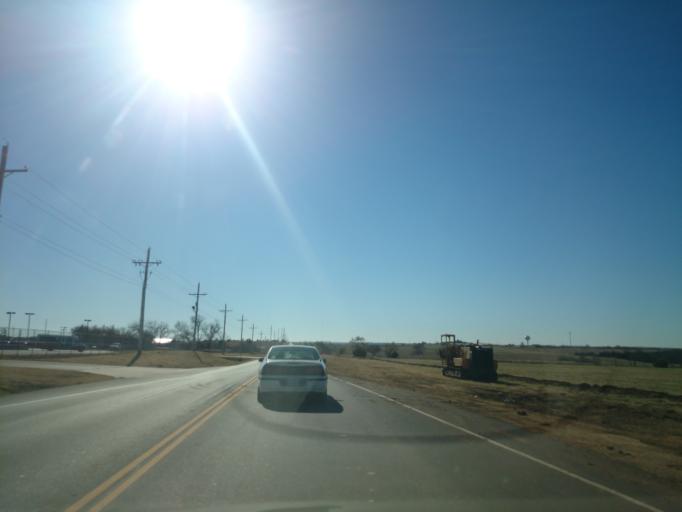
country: US
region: Oklahoma
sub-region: Payne County
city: Stillwater
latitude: 36.1447
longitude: -97.0875
